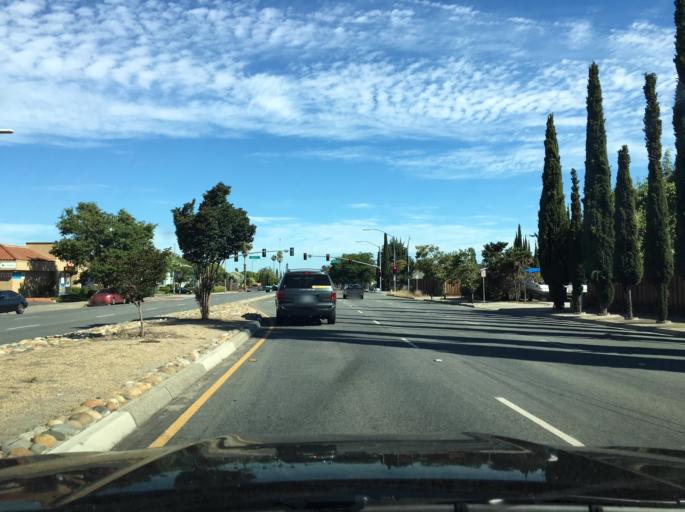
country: US
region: California
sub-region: Santa Clara County
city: Cambrian Park
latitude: 37.2421
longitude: -121.9051
